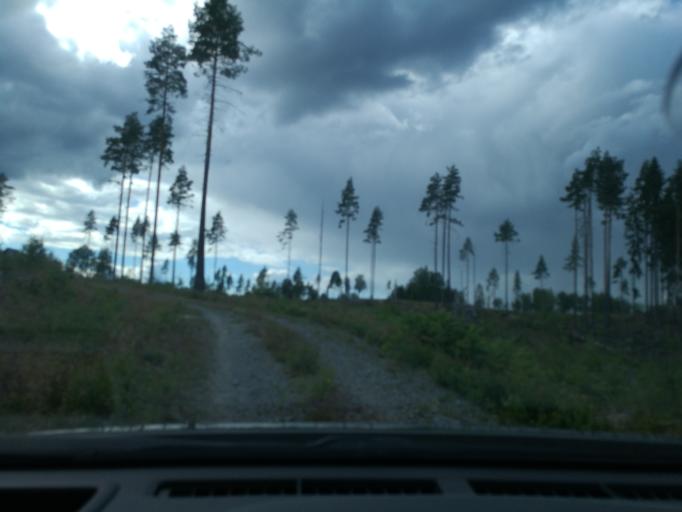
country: SE
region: Vaestmanland
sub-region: Surahammars Kommun
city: Ramnas
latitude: 59.8026
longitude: 16.2898
